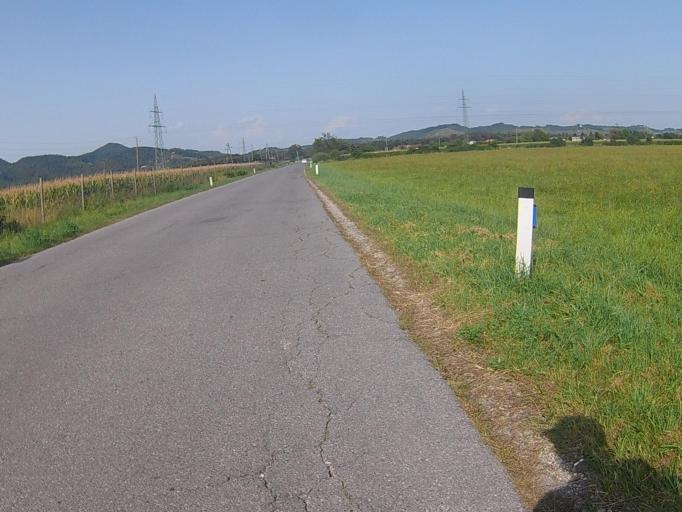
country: SI
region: Maribor
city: Pekre
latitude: 46.5524
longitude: 15.5980
